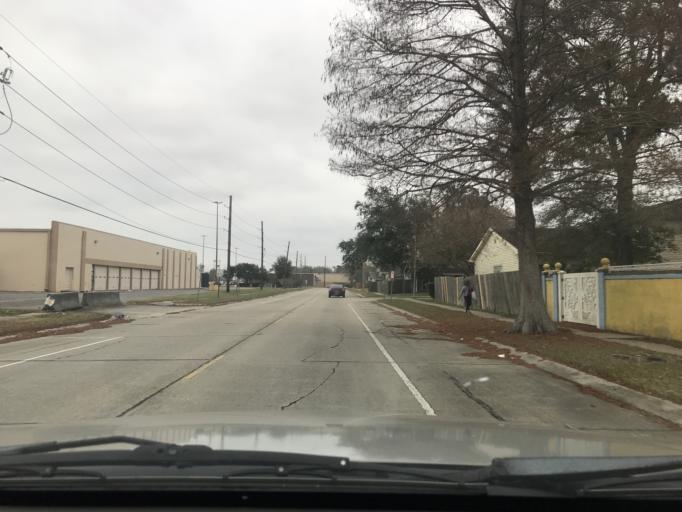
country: US
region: Louisiana
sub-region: Jefferson Parish
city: Woodmere
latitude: 29.8677
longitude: -90.0795
